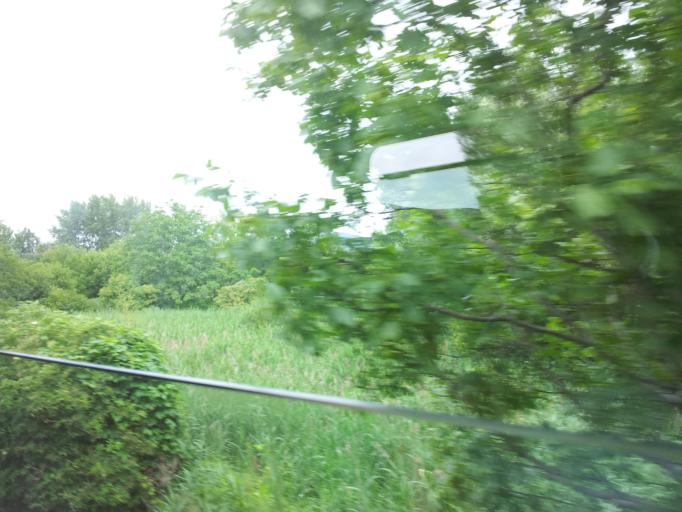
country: HU
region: Veszprem
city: Badacsonytomaj
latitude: 46.8043
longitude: 17.4686
